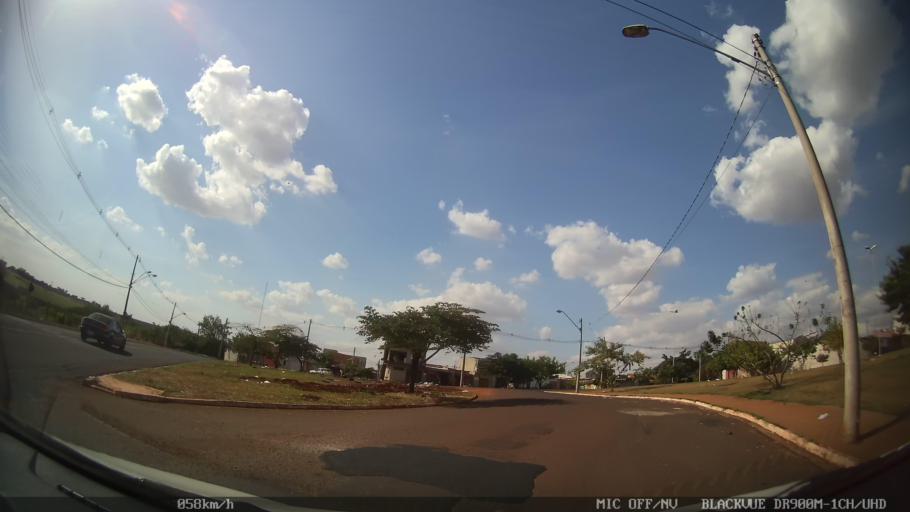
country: BR
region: Sao Paulo
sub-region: Ribeirao Preto
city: Ribeirao Preto
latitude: -21.2021
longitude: -47.8580
